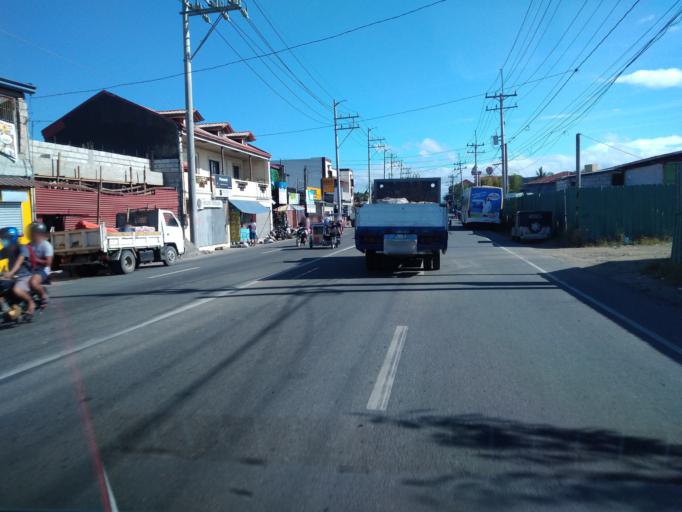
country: PH
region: Central Luzon
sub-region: Province of Bulacan
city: Santa Maria
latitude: 14.8191
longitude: 120.9506
